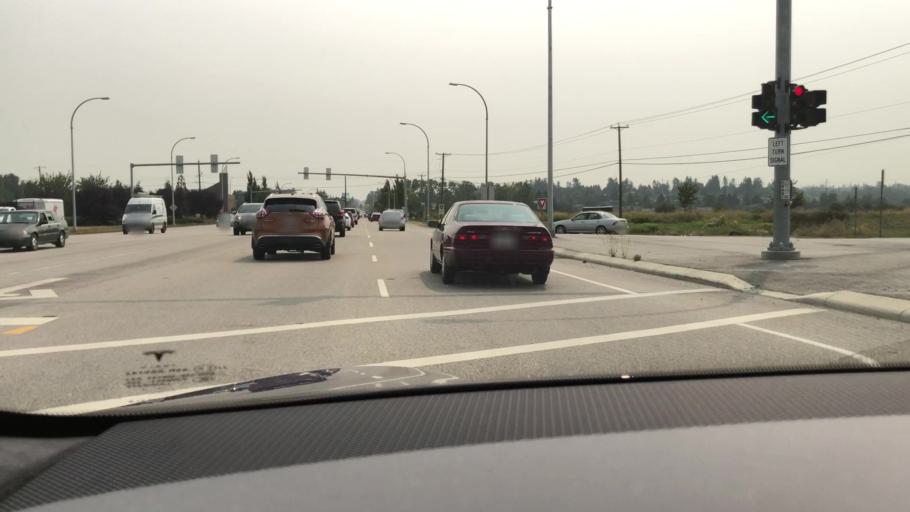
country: CA
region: British Columbia
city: Ladner
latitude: 49.0421
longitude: -123.0675
